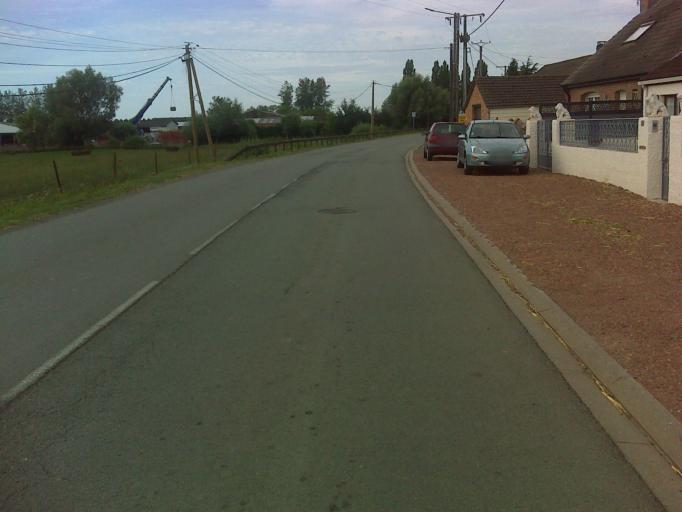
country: FR
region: Nord-Pas-de-Calais
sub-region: Departement du Nord
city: Crespin
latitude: 50.4447
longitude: 3.6456
